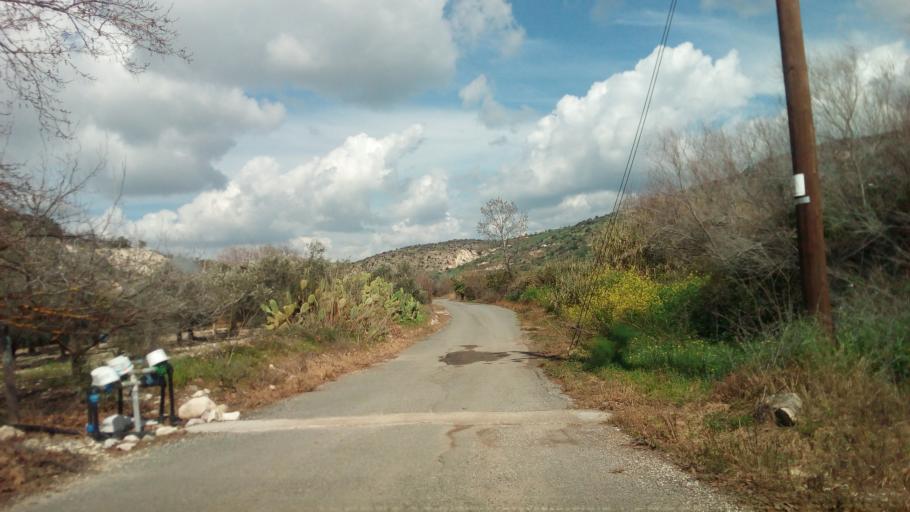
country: CY
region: Pafos
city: Mesogi
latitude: 34.8009
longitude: 32.5291
